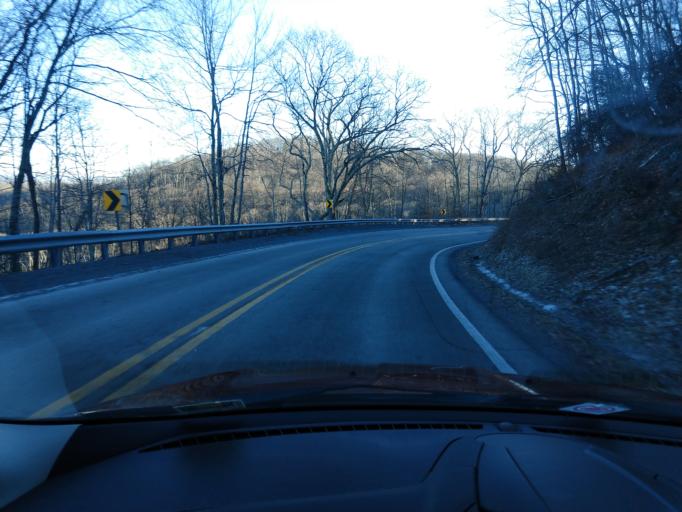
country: US
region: Virginia
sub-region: Highland County
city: Monterey
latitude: 38.4878
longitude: -79.7012
